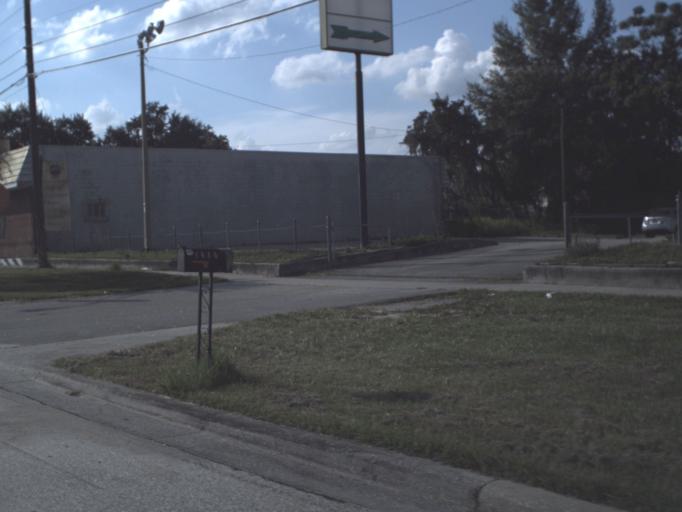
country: US
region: Florida
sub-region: Polk County
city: Lakeland
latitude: 28.0549
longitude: -81.9767
